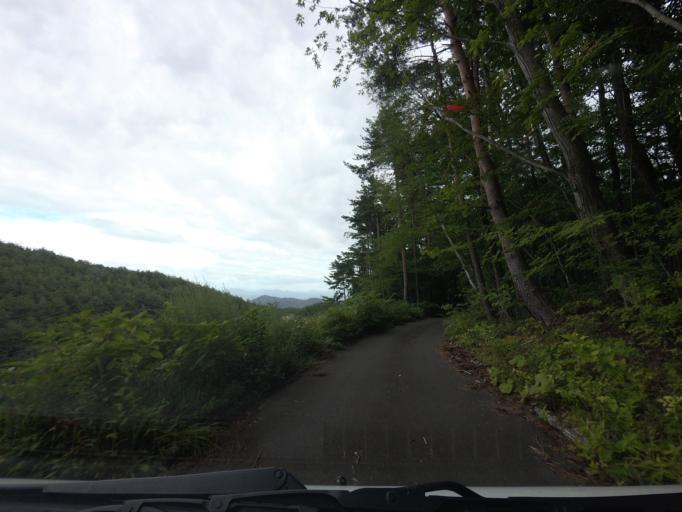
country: JP
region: Fukushima
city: Motomiya
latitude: 37.5621
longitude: 140.3038
